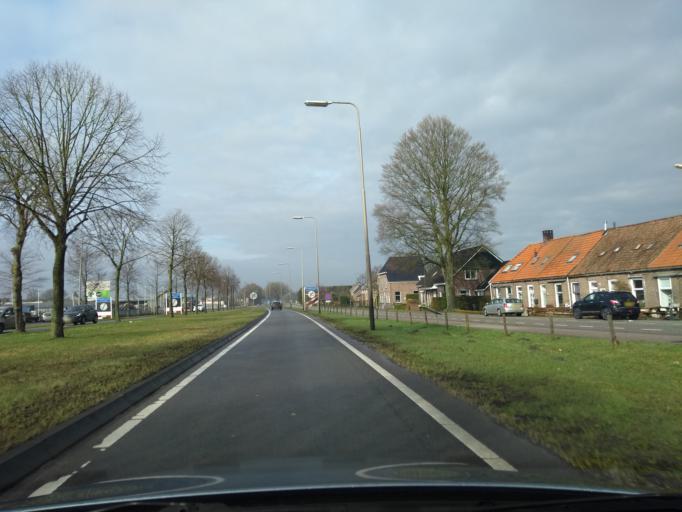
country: NL
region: Overijssel
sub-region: Gemeente Staphorst
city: Staphorst
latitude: 52.5925
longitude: 6.2649
